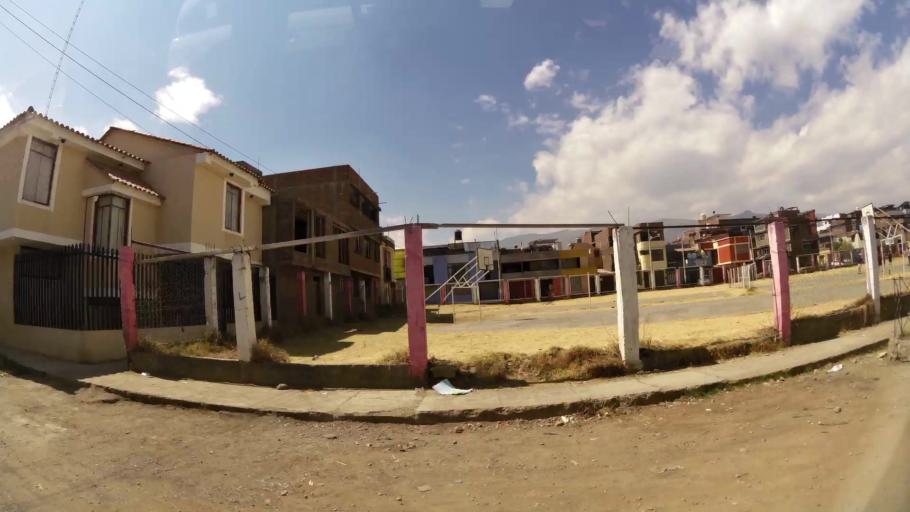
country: PE
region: Junin
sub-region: Provincia de Huancayo
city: El Tambo
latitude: -12.0661
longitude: -75.2212
